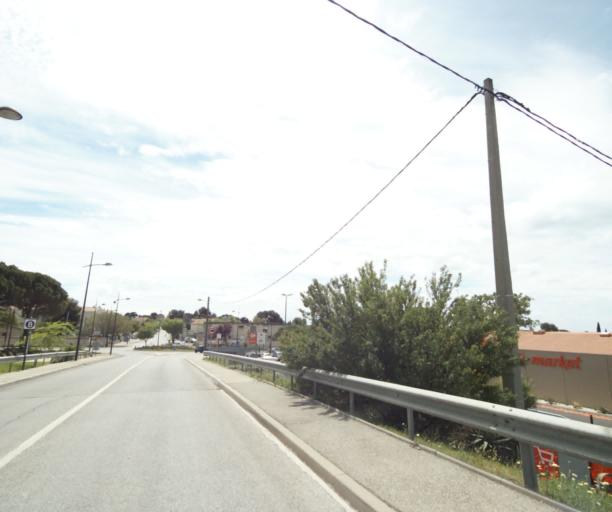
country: FR
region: Provence-Alpes-Cote d'Azur
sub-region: Departement des Bouches-du-Rhone
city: Rognac
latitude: 43.4925
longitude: 5.2295
